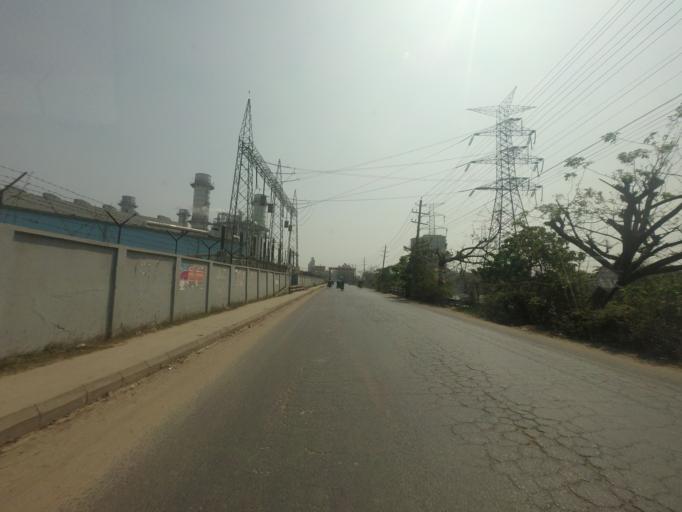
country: BD
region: Dhaka
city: Bhairab Bazar
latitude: 24.0375
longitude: 91.0064
